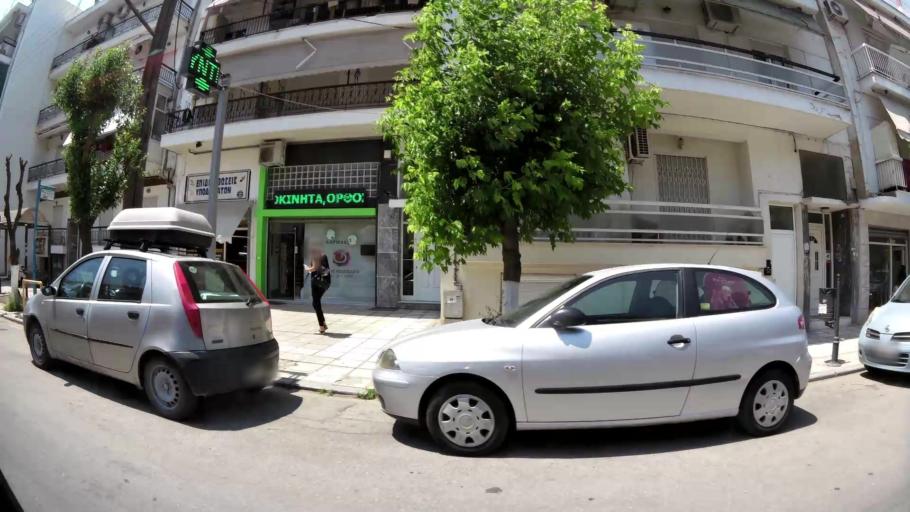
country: GR
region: Central Macedonia
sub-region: Nomos Thessalonikis
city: Ampelokipoi
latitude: 40.6522
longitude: 22.9314
